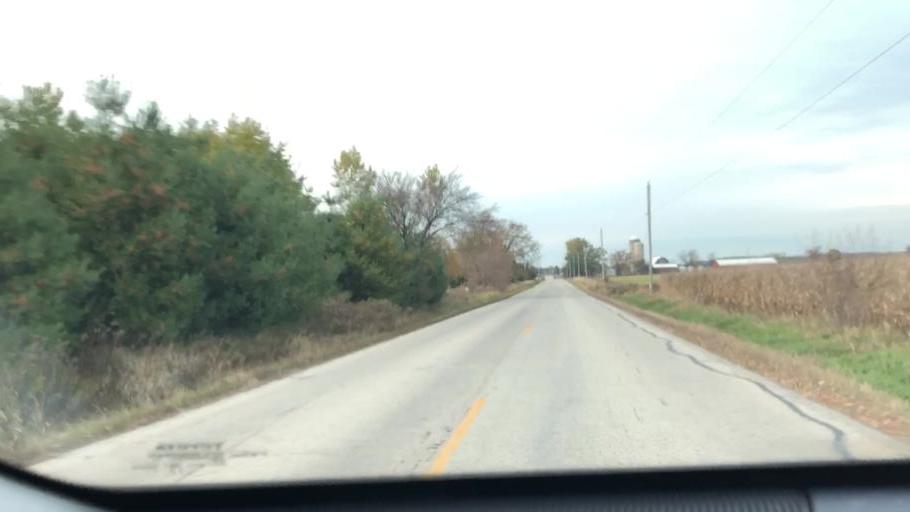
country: US
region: Wisconsin
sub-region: Outagamie County
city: Seymour
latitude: 44.4547
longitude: -88.3500
